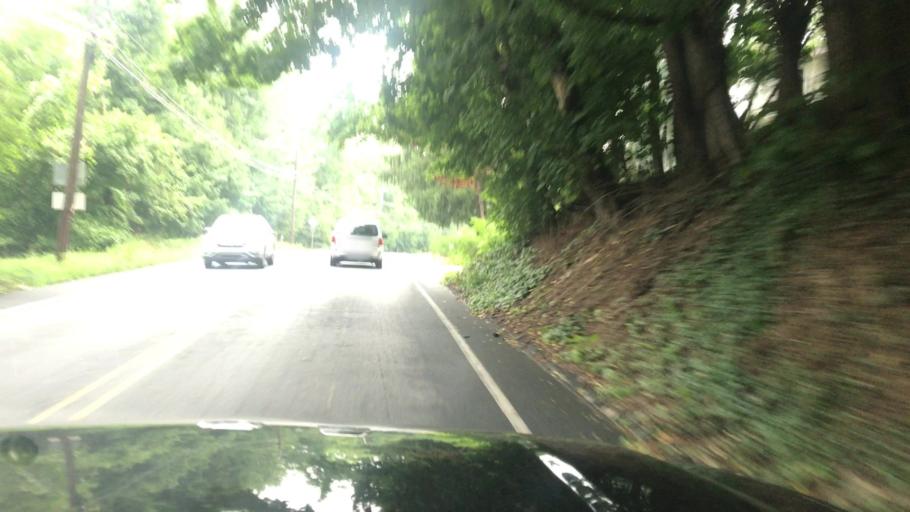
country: US
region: Pennsylvania
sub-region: Cumberland County
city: Shiremanstown
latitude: 40.2409
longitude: -76.9519
